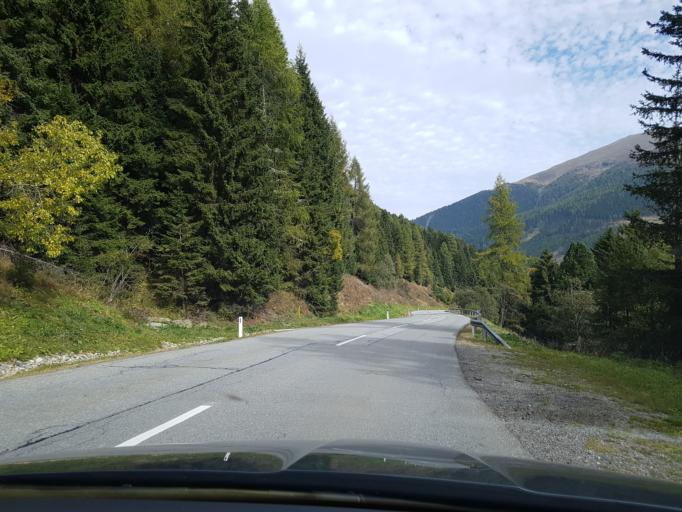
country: AT
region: Carinthia
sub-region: Politischer Bezirk Spittal an der Drau
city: Kleinkirchheim
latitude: 46.9342
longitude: 13.8748
